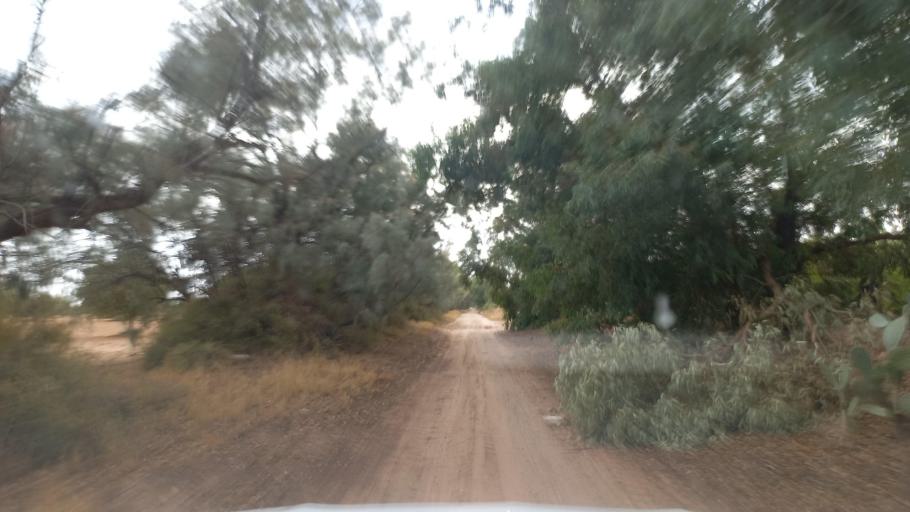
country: TN
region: Al Qasrayn
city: Sbiba
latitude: 35.2944
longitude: 9.0661
